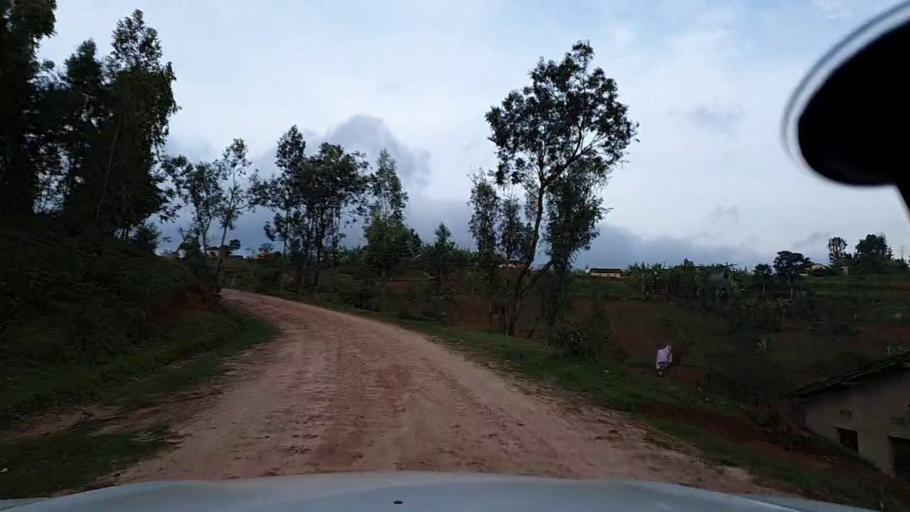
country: RW
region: Southern Province
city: Gitarama
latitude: -2.2086
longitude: 29.6034
